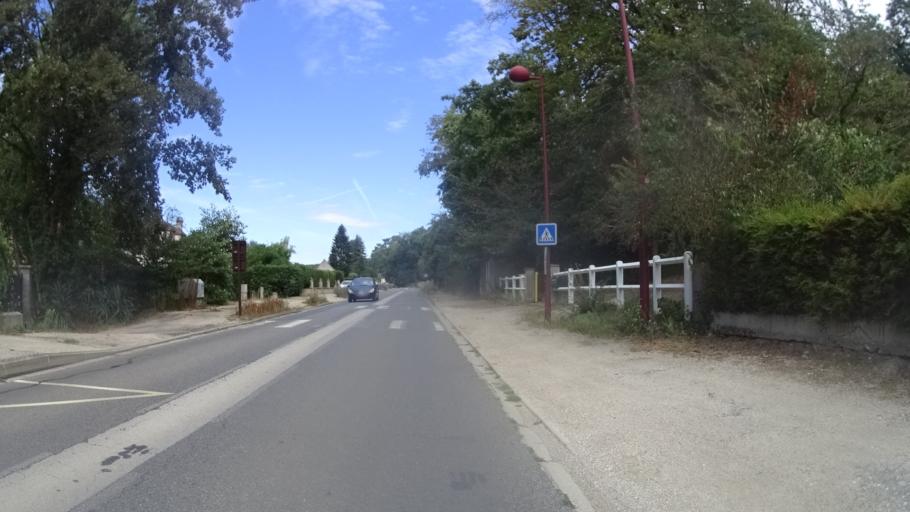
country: FR
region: Centre
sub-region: Departement du Loiret
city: Malesherbes
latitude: 48.2816
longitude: 2.4256
